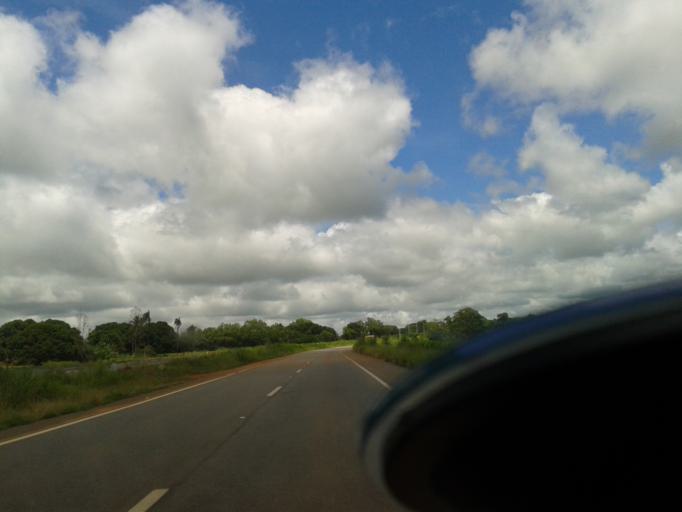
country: BR
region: Goias
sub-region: Itaberai
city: Itaberai
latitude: -16.0695
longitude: -49.7678
